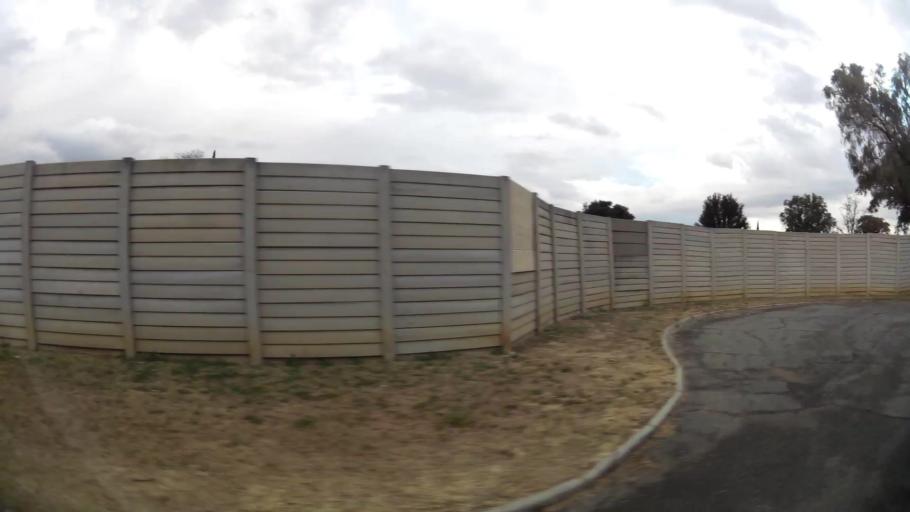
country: ZA
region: Orange Free State
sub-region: Lejweleputswa District Municipality
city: Welkom
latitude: -27.9561
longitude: 26.7395
